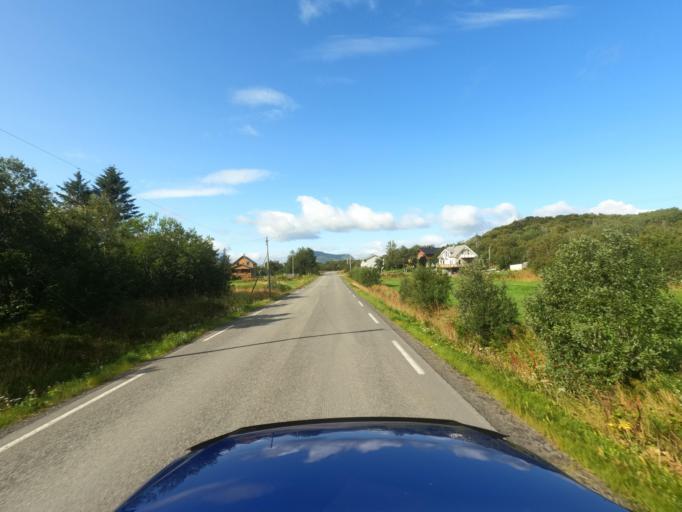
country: NO
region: Nordland
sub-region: Vestvagoy
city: Leknes
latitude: 68.1247
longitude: 13.6414
